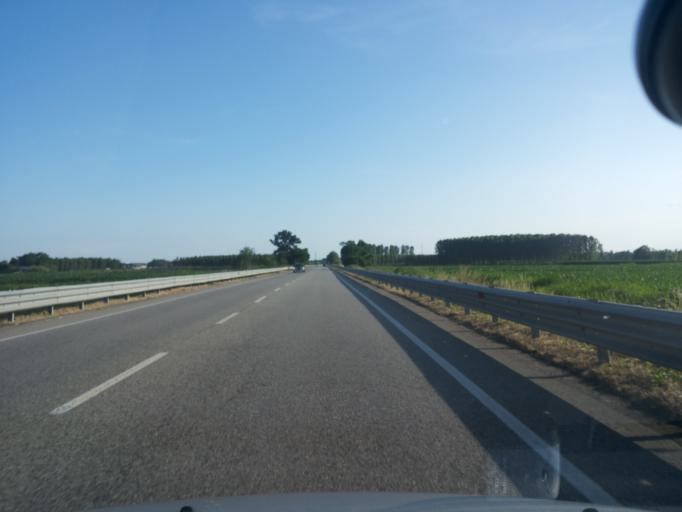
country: IT
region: Piedmont
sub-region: Provincia di Vercelli
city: Borgo Vercelli
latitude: 45.3575
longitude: 8.4544
